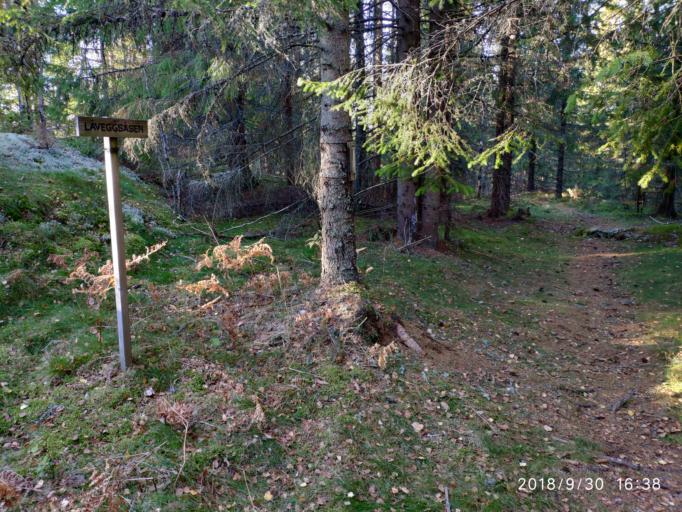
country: NO
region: Akershus
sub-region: Nes
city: Neskollen
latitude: 60.2011
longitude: 11.3193
